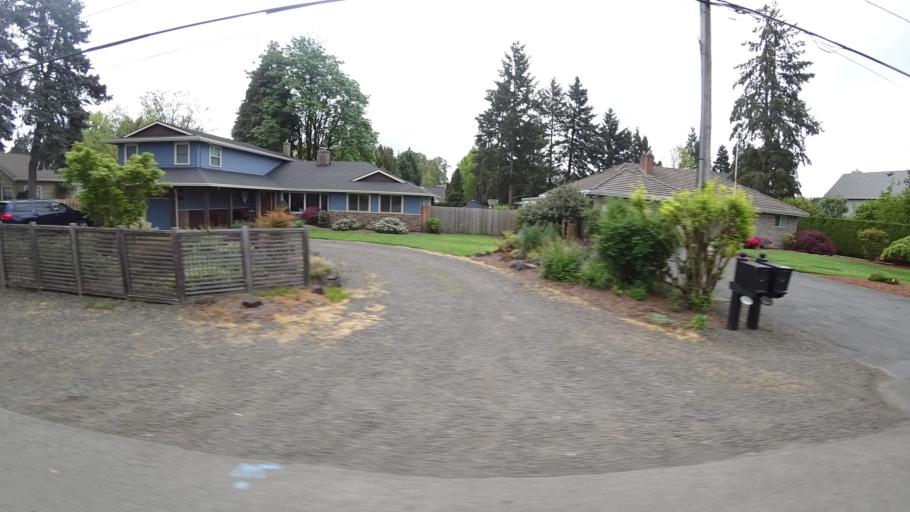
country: US
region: Oregon
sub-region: Washington County
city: Hillsboro
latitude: 45.5449
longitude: -122.9797
